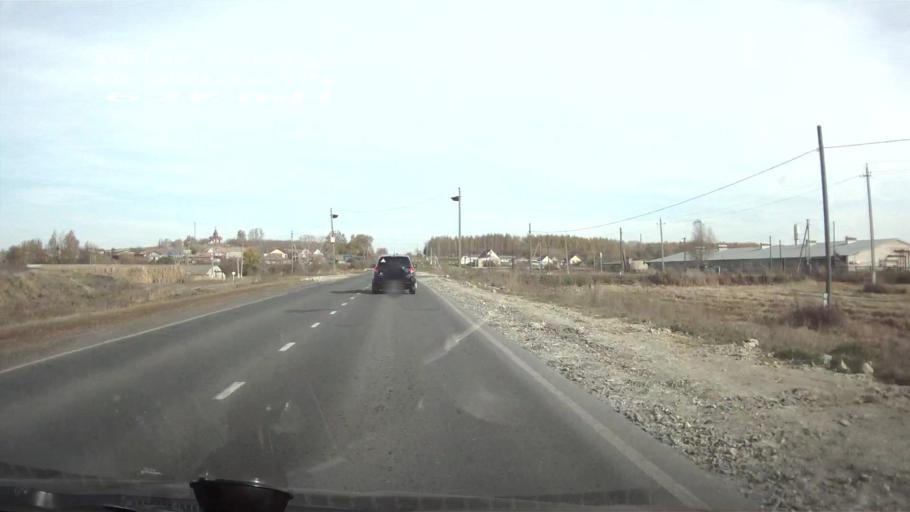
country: RU
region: Mordoviya
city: Atyashevo
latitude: 54.5603
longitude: 45.9761
